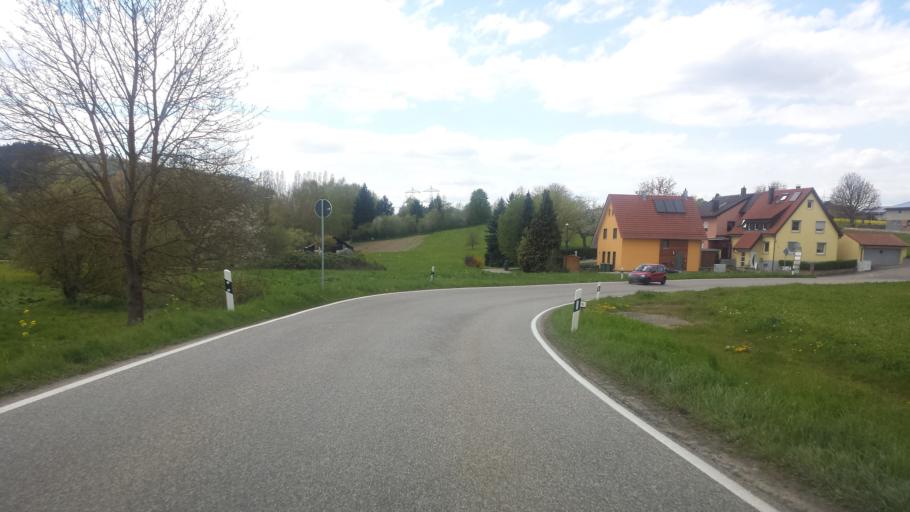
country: DE
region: Baden-Wuerttemberg
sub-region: Karlsruhe Region
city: Muhlacker
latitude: 48.9308
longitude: 8.8407
